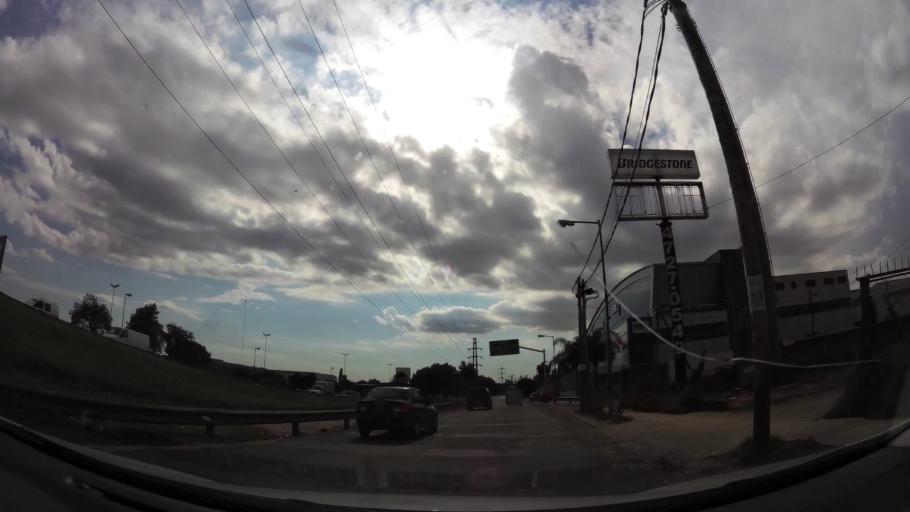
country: AR
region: Buenos Aires
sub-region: Partido de Tigre
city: Tigre
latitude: -34.4816
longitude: -58.6350
